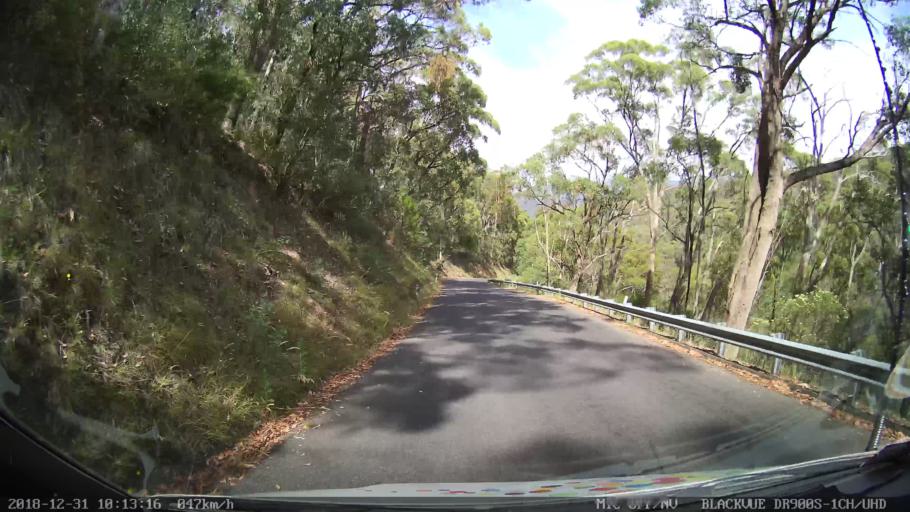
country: AU
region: New South Wales
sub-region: Snowy River
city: Jindabyne
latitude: -36.5377
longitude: 148.1562
